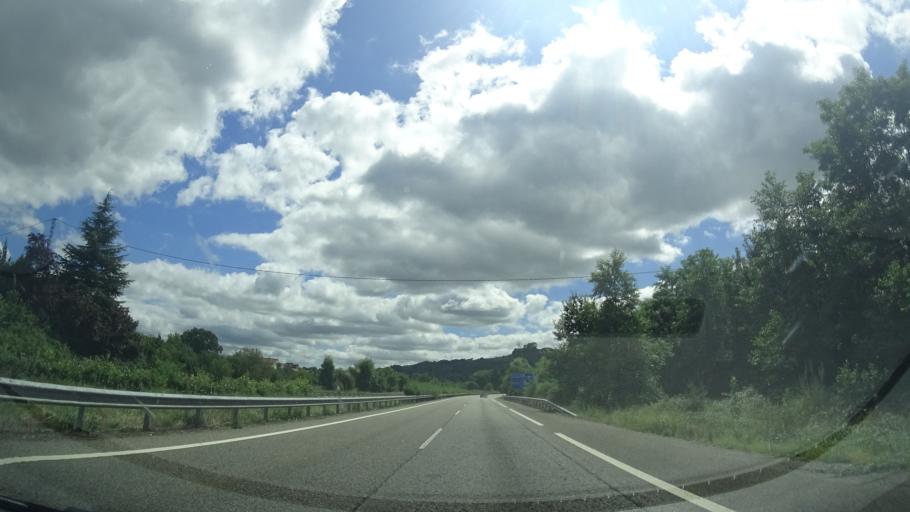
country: ES
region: Asturias
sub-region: Province of Asturias
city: Pola de Siero
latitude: 43.3813
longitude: -5.6124
